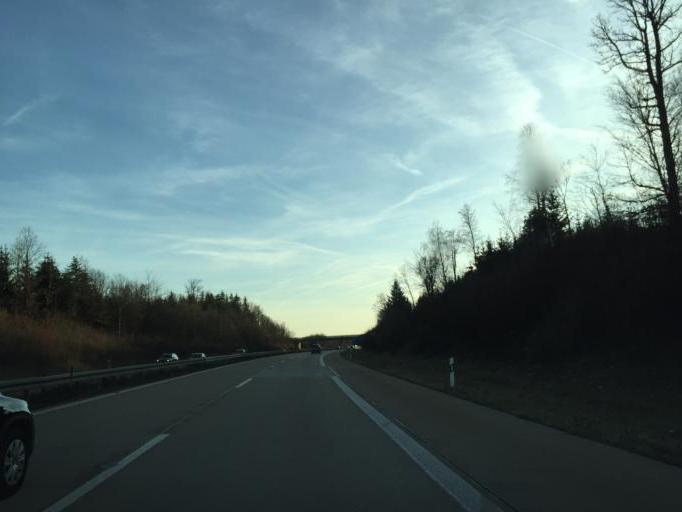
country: DE
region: Bavaria
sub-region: Regierungsbezirk Mittelfranken
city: Schillingsfurst
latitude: 49.2723
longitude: 10.2361
